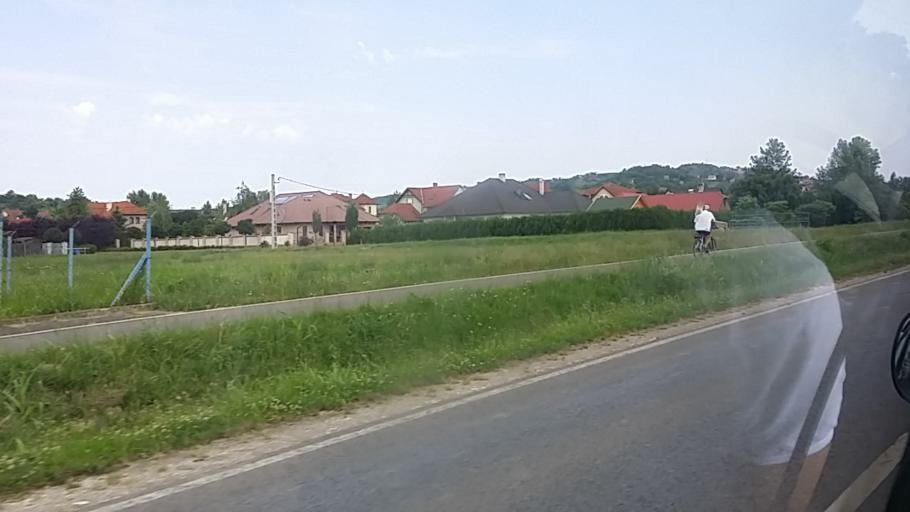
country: HU
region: Tolna
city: Szekszard
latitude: 46.3220
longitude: 18.6976
